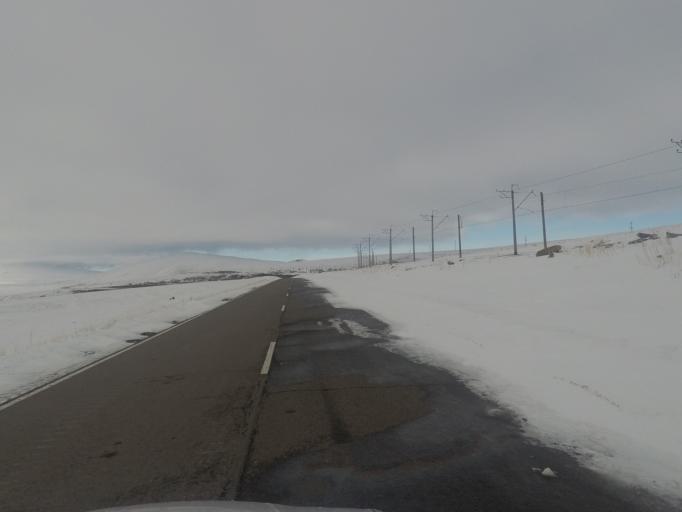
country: GE
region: Kvemo Kartli
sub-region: Tsalka
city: Tsalka
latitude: 41.4372
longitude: 43.8453
